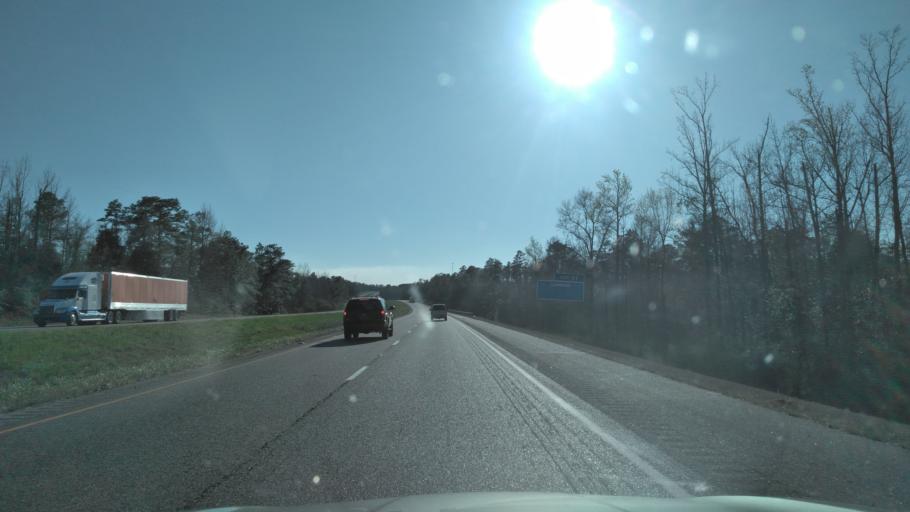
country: US
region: Alabama
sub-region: Escambia County
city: Atmore
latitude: 31.1266
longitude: -87.4444
